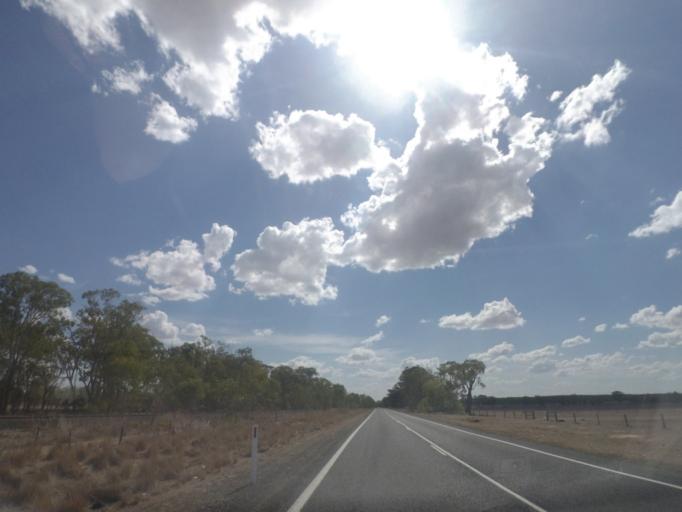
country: AU
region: Queensland
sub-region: Southern Downs
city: Stanthorpe
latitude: -28.3943
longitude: 151.3125
